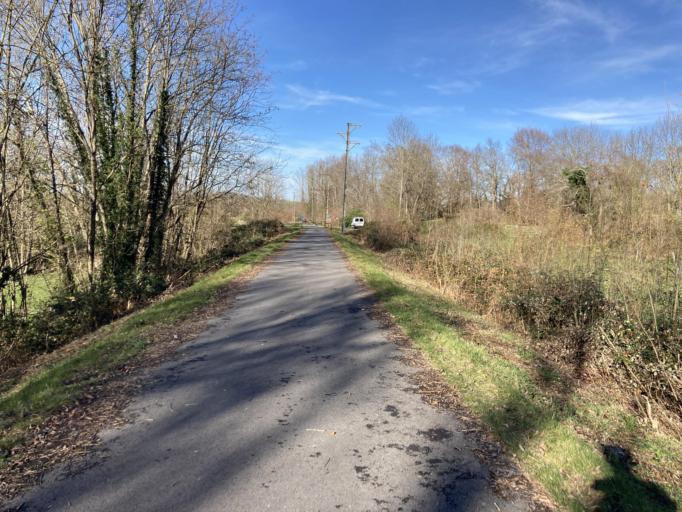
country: FR
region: Aquitaine
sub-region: Departement des Pyrenees-Atlantiques
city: Arudy
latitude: 43.1375
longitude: -0.4473
